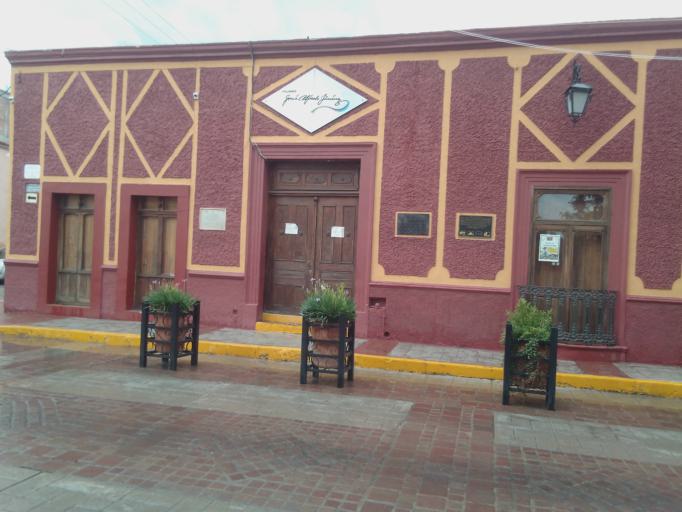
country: MX
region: Guanajuato
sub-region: Dolores Hidalgo Cuna de la Independencia Nacional
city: Dolores Hidalgo Cuna de la Independencia Nacional
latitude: 21.1573
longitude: -100.9328
